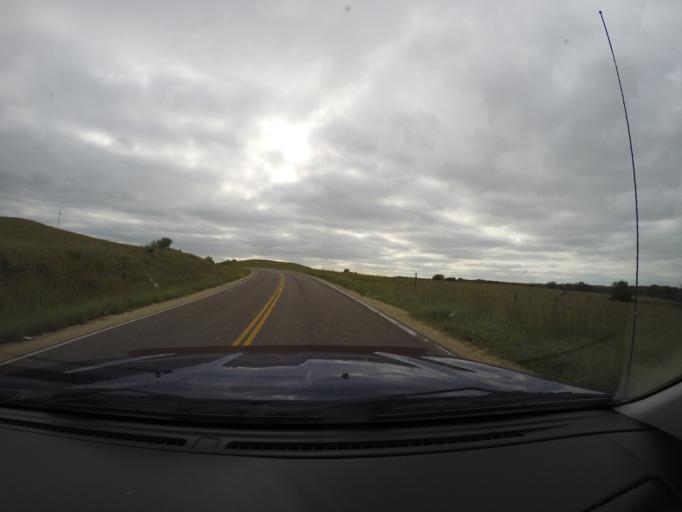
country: US
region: Kansas
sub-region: Dickinson County
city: Herington
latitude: 38.7991
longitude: -96.9325
